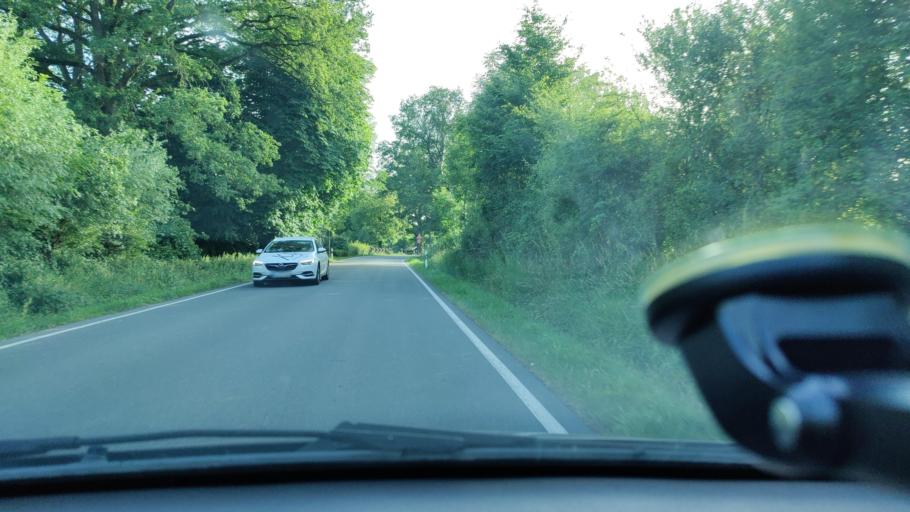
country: DE
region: North Rhine-Westphalia
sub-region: Regierungsbezirk Munster
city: Billerbeck
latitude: 51.9955
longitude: 7.2417
